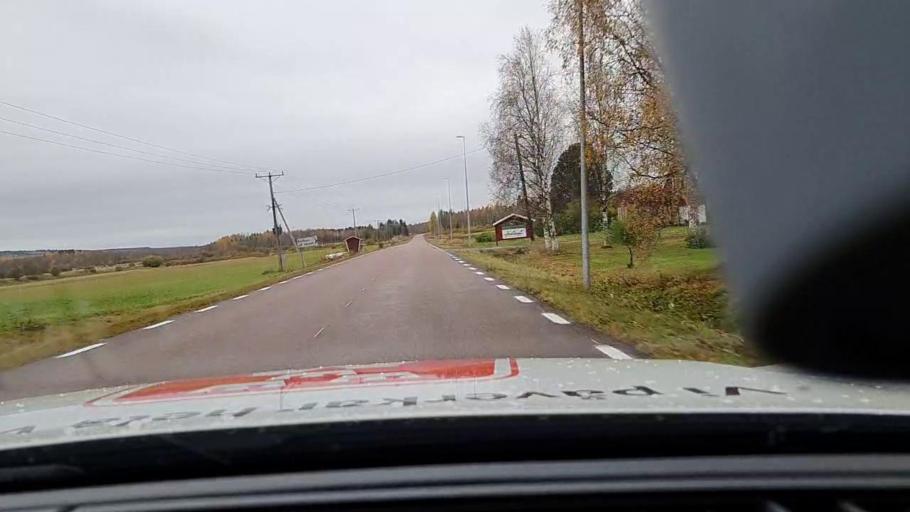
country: FI
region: Lapland
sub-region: Torniolaakso
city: Ylitornio
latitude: 66.1338
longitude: 23.9055
